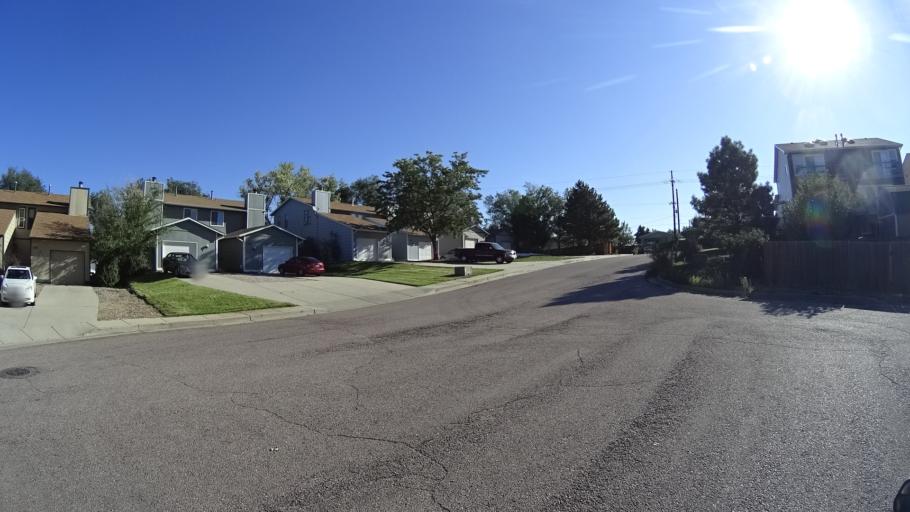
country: US
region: Colorado
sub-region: El Paso County
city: Colorado Springs
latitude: 38.8431
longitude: -104.8414
